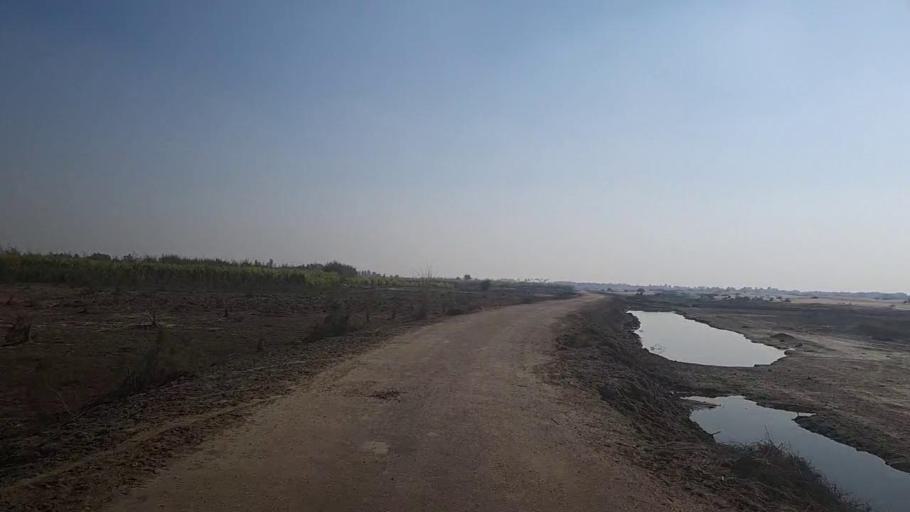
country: PK
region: Sindh
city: Khairpur
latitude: 27.4392
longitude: 68.7278
